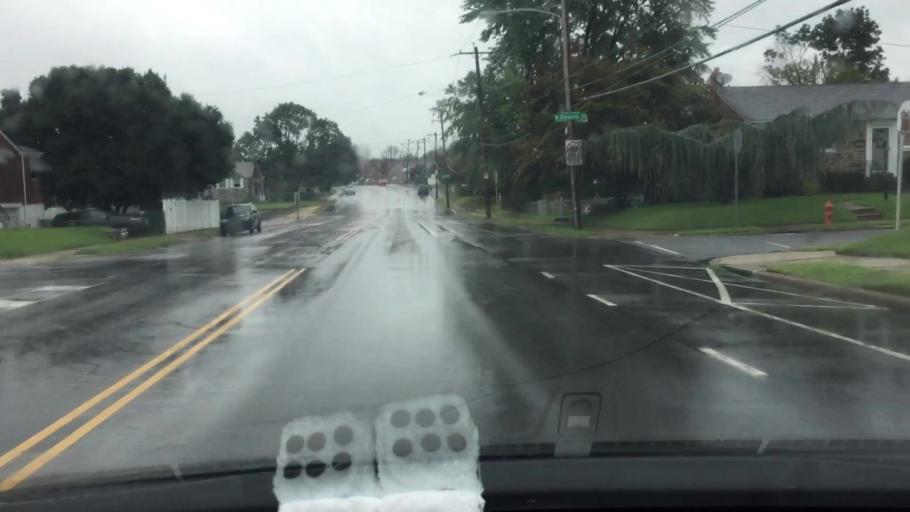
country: US
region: New Jersey
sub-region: Burlington County
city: Palmyra
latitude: 40.0514
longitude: -75.0465
